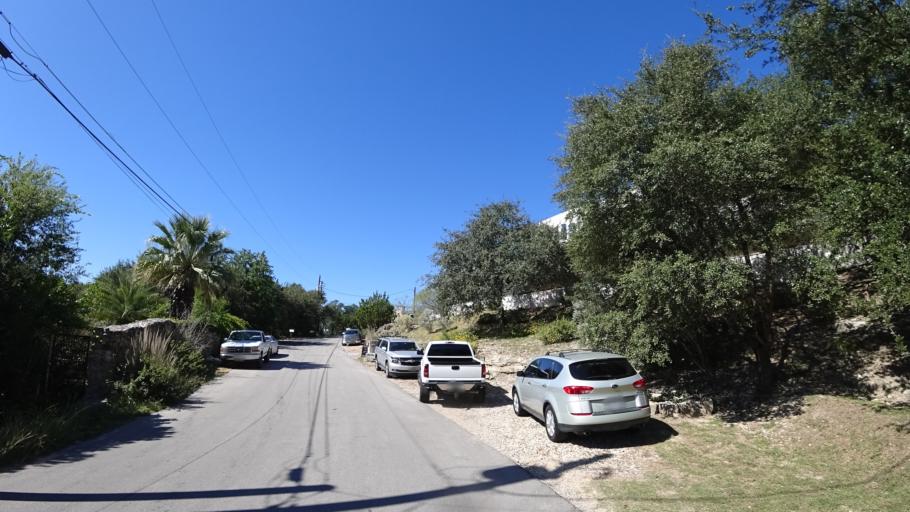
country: US
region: Texas
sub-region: Travis County
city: West Lake Hills
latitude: 30.3110
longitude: -97.8035
